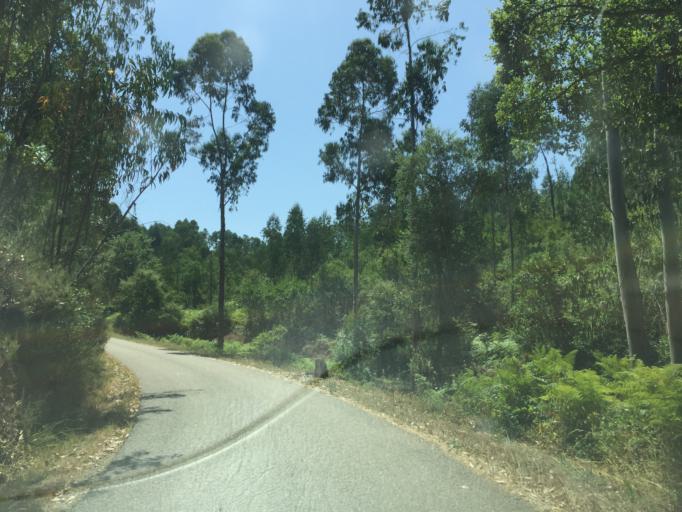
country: PT
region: Santarem
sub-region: Ferreira do Zezere
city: Ferreira do Zezere
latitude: 39.6492
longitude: -8.3020
